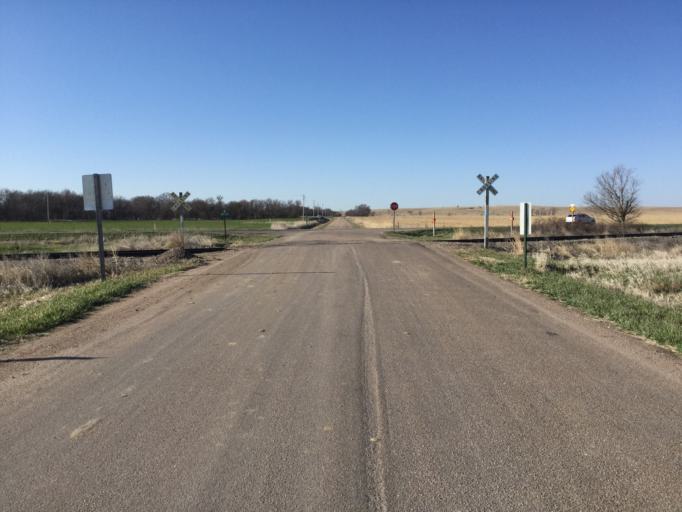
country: US
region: Kansas
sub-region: Norton County
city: Norton
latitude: 39.8766
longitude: -99.7210
